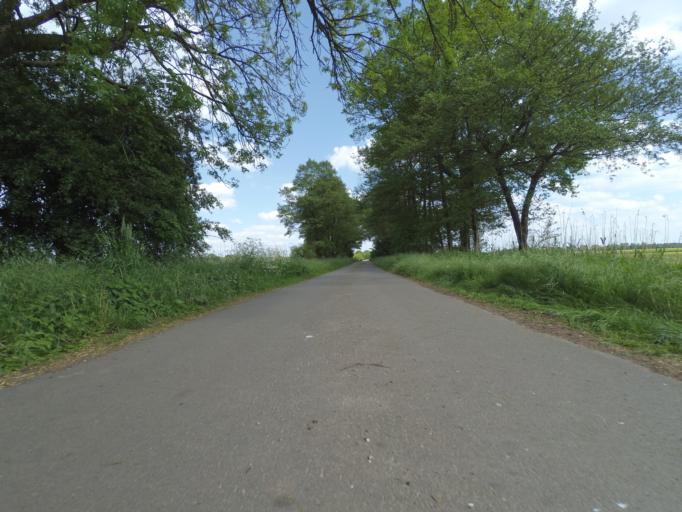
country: DE
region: Lower Saxony
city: Haenigsen
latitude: 52.5130
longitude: 10.0745
